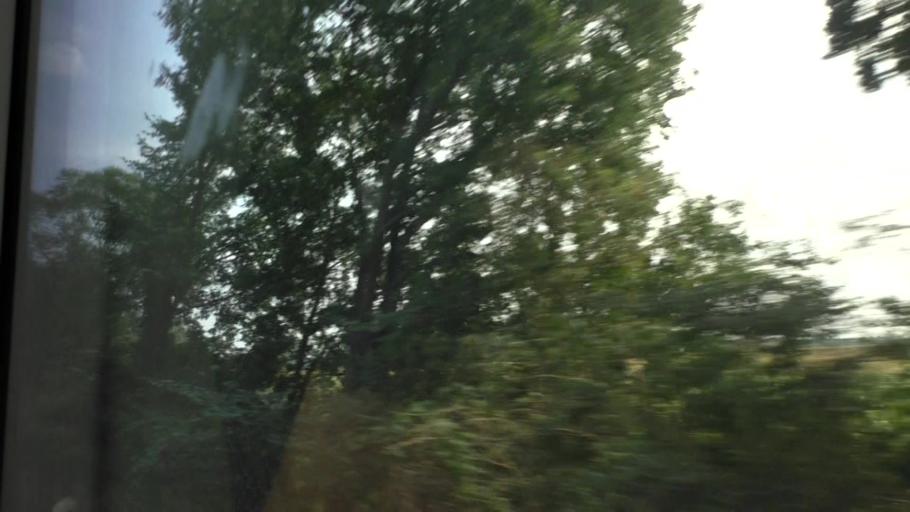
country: DE
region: Brandenburg
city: Beeskow
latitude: 52.1705
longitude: 14.3043
